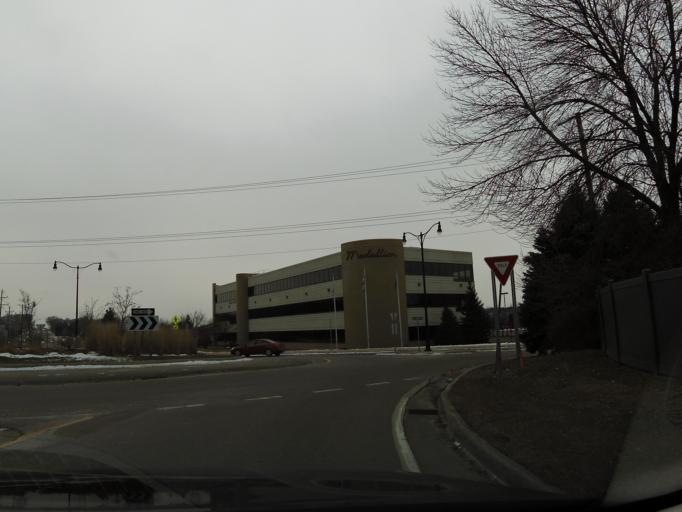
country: US
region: Minnesota
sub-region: Carver County
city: Waconia
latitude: 44.8403
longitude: -93.7885
